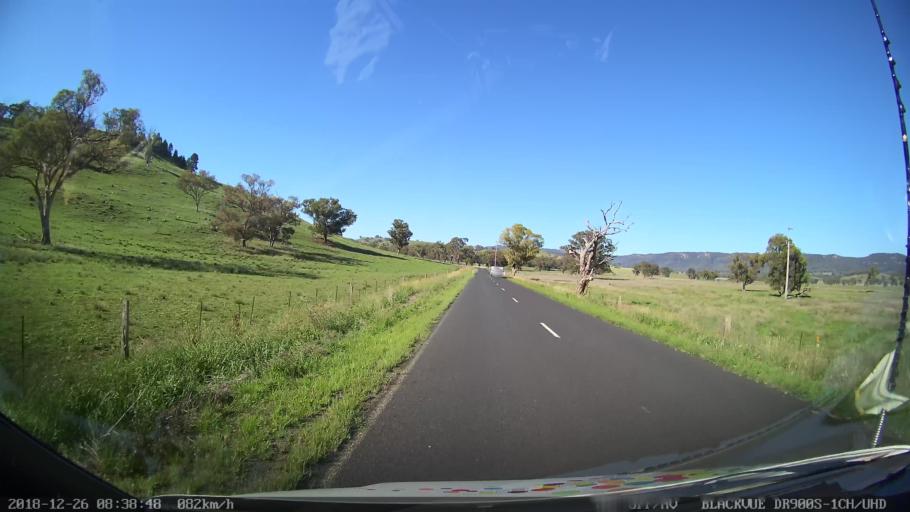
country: AU
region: New South Wales
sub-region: Upper Hunter Shire
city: Merriwa
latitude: -32.4466
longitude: 150.0796
